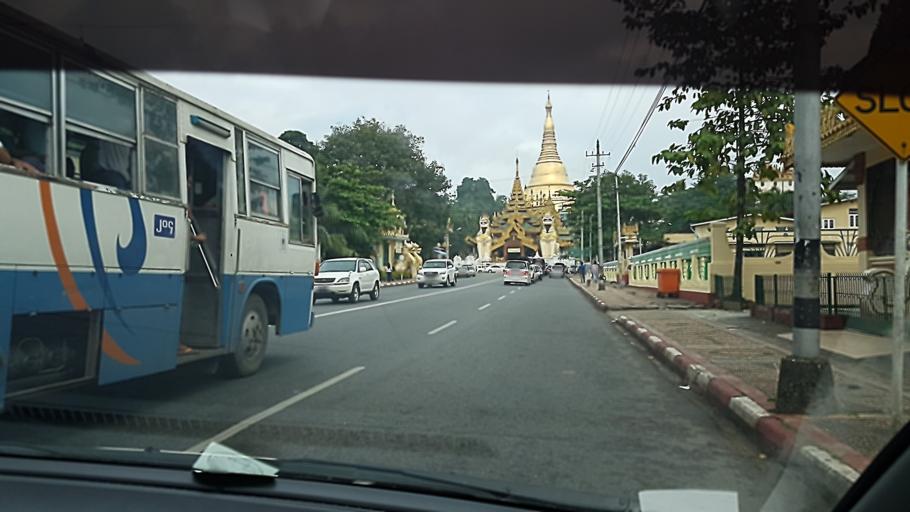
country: MM
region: Yangon
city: Yangon
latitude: 16.7942
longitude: 96.1509
